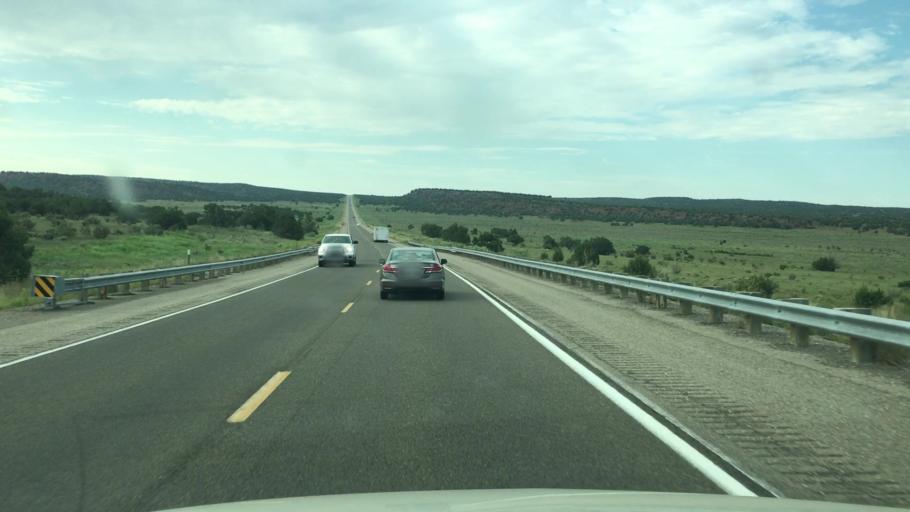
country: US
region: New Mexico
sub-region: Santa Fe County
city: Eldorado at Santa Fe
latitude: 35.2547
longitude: -105.8086
